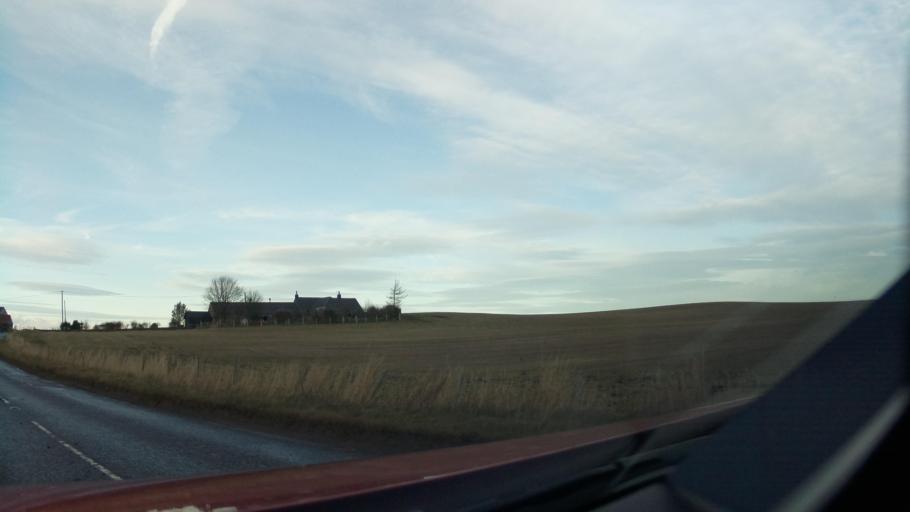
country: GB
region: Scotland
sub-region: Angus
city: Letham
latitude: 56.5707
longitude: -2.7790
